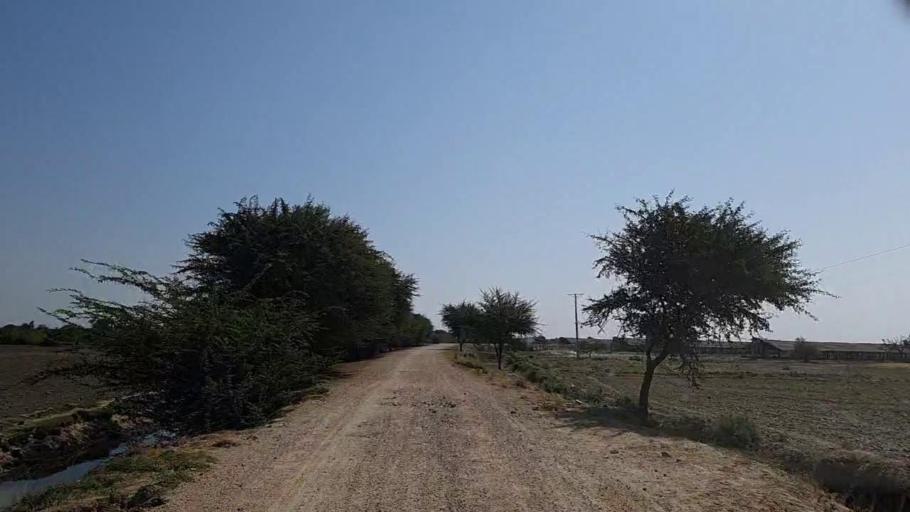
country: PK
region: Sindh
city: Mirpur Batoro
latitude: 24.6798
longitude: 68.2992
